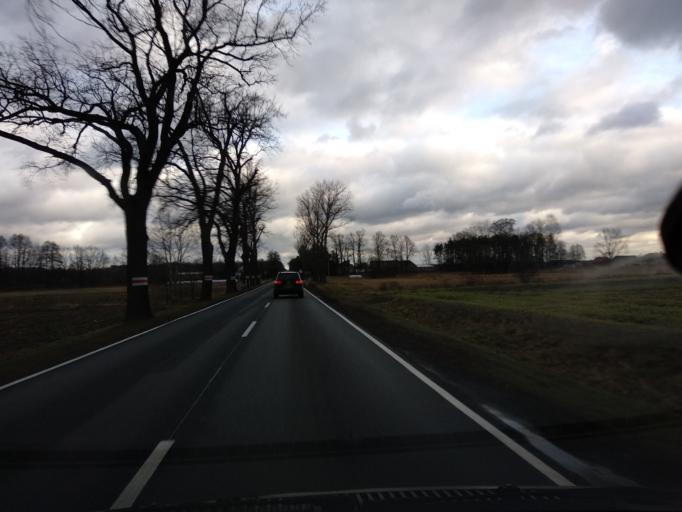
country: PL
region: Greater Poland Voivodeship
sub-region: Powiat ostrowski
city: Jankow Przygodzki
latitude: 51.4842
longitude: 17.7640
